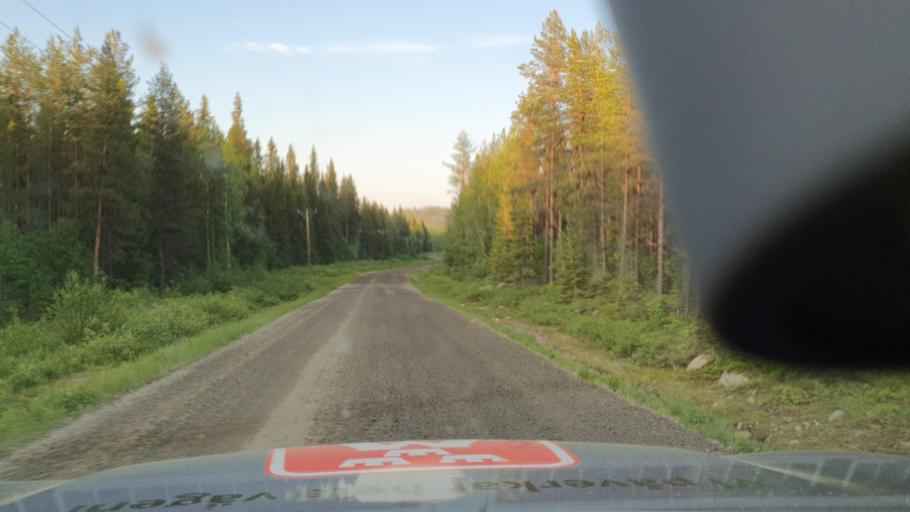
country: SE
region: Norrbotten
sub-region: Bodens Kommun
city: Boden
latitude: 66.0793
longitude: 21.6615
